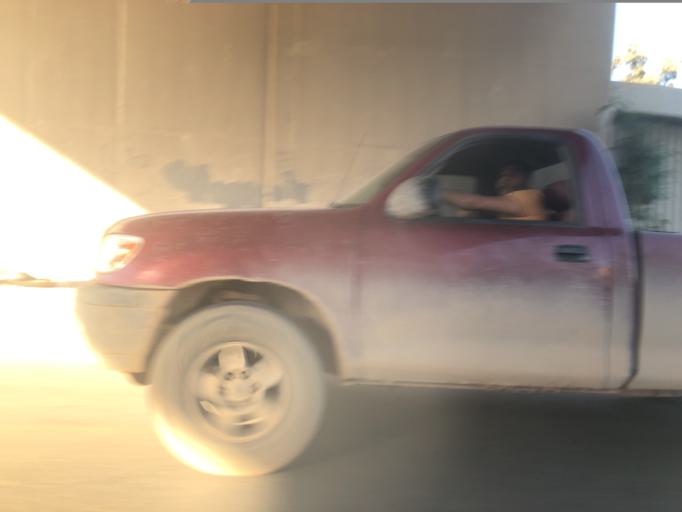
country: LY
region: Tripoli
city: Tagiura
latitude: 32.8691
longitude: 13.2752
